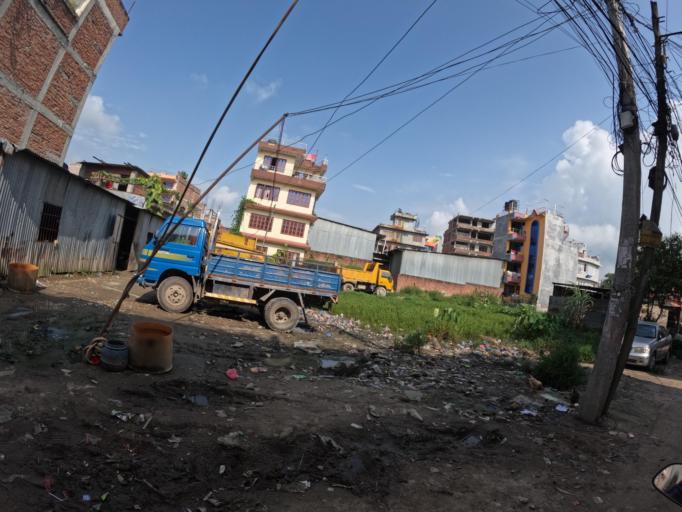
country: NP
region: Central Region
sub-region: Bagmati Zone
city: Bhaktapur
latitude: 27.6808
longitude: 85.4456
